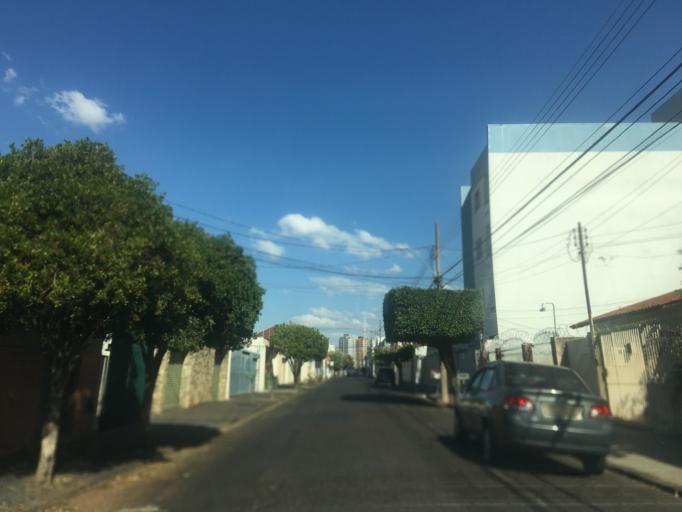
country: BR
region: Minas Gerais
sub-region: Uberlandia
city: Uberlandia
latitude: -18.9091
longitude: -48.2814
